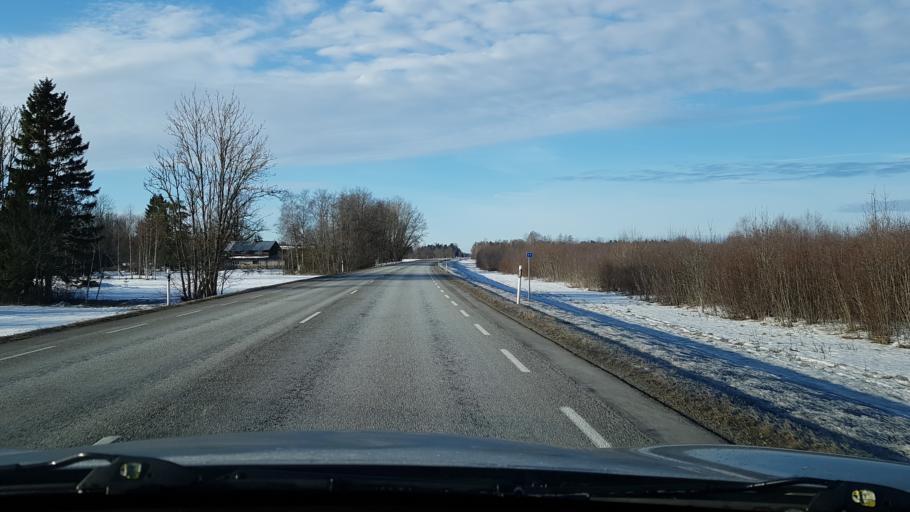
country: EE
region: Viljandimaa
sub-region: Vohma linn
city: Vohma
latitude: 58.6730
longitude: 25.6586
